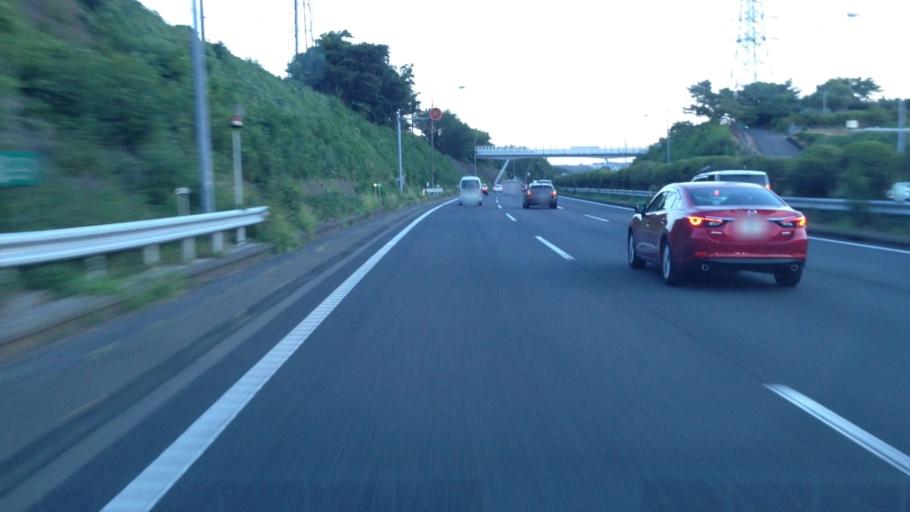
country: JP
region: Kanagawa
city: Yokohama
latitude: 35.5347
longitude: 139.6009
